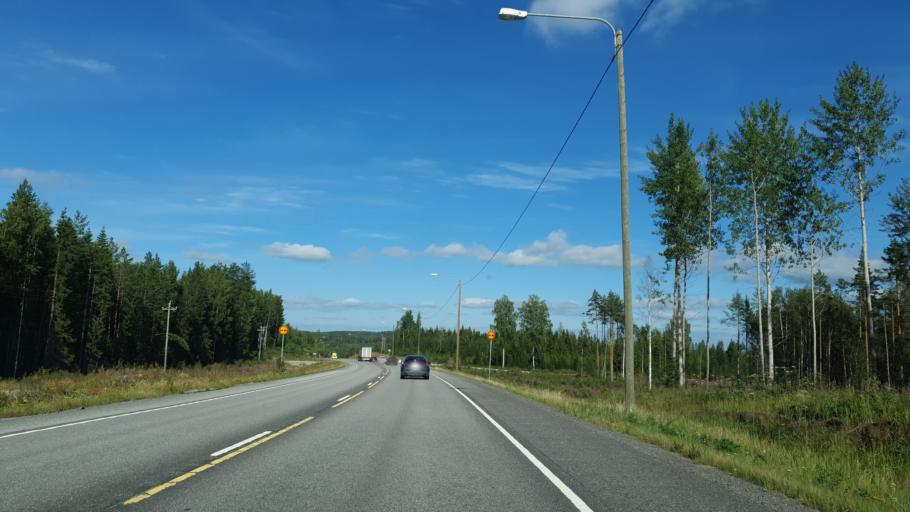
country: FI
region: Central Finland
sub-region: Jyvaeskylae
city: Toivakka
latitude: 62.2478
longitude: 26.0551
